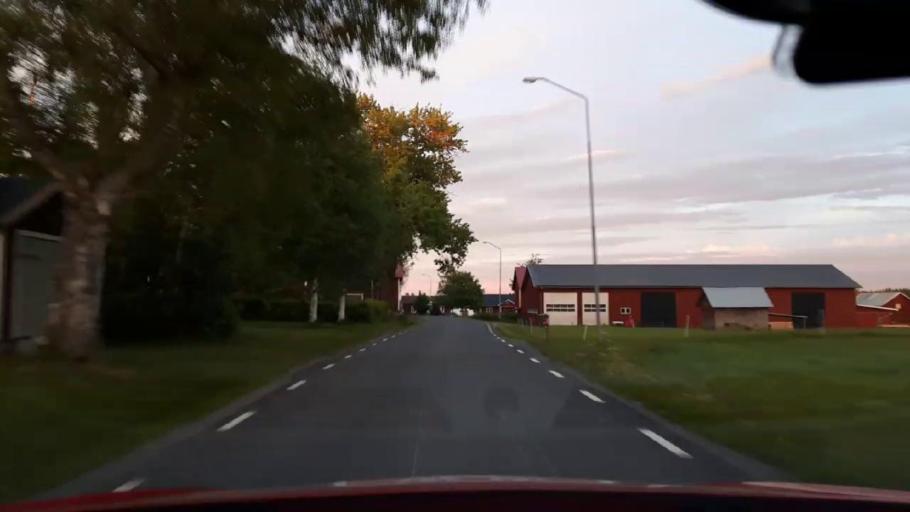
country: SE
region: Jaemtland
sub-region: OEstersunds Kommun
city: Brunflo
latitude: 63.0573
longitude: 14.8112
